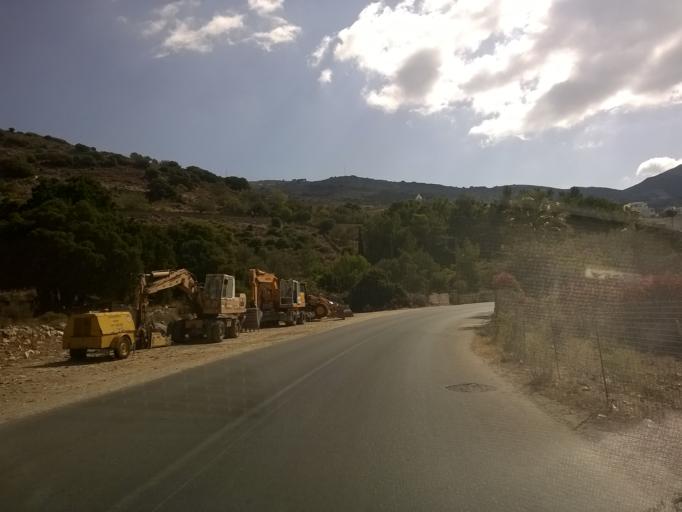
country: GR
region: South Aegean
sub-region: Nomos Kykladon
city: Filotion
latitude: 37.0572
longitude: 25.4966
